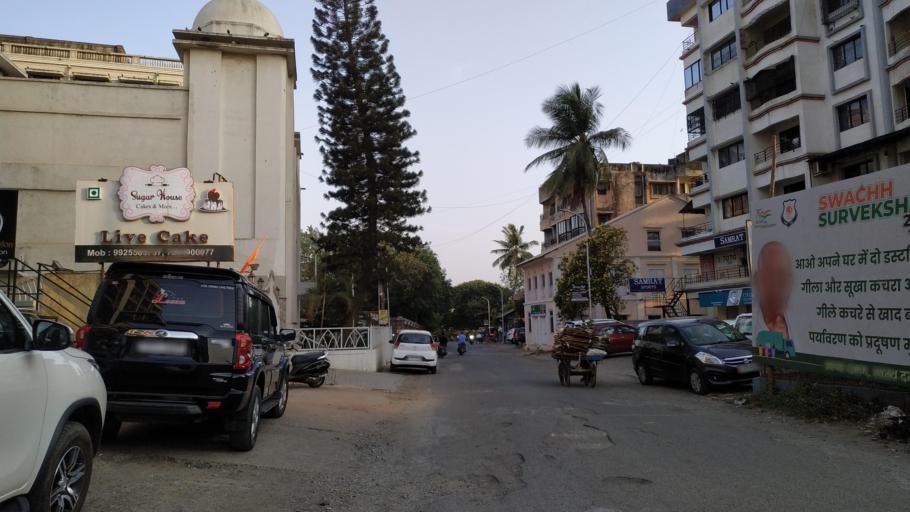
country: IN
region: Daman and Diu
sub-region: Daman District
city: Daman
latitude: 20.4148
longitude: 72.8336
